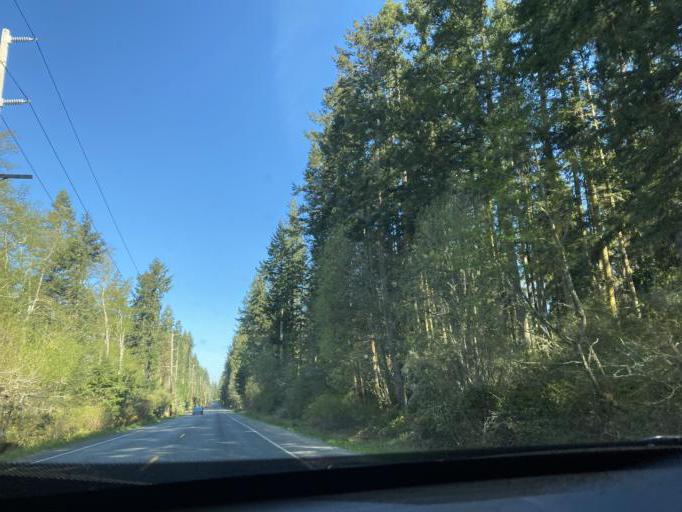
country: US
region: Washington
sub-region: Island County
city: Freeland
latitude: 48.0628
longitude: -122.5963
